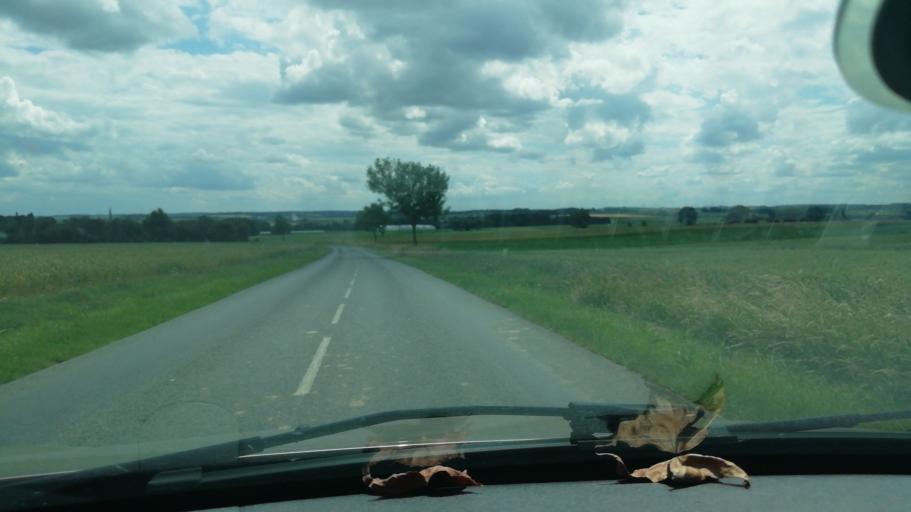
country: FR
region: Nord-Pas-de-Calais
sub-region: Departement du Pas-de-Calais
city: Aubigny-en-Artois
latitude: 50.3335
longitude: 2.5874
